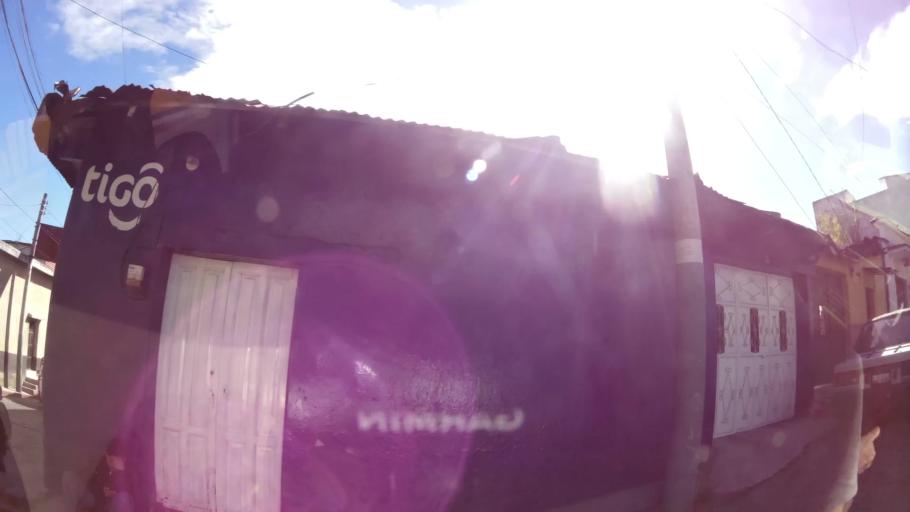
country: GT
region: Solola
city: Solola
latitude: 14.7708
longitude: -91.1812
